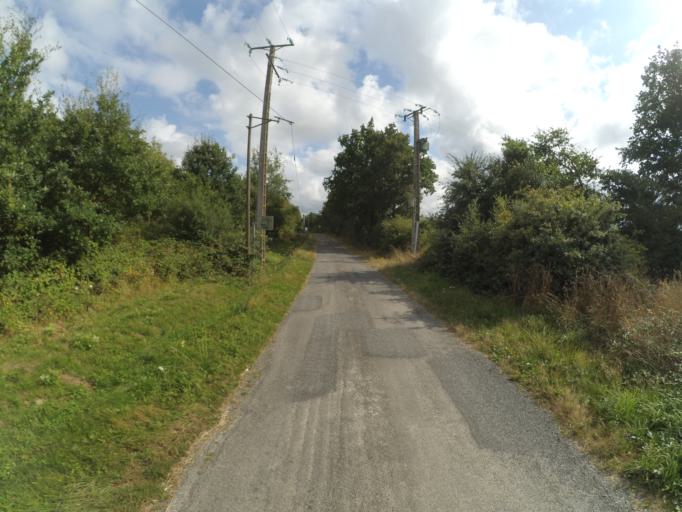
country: FR
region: Pays de la Loire
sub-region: Departement de la Loire-Atlantique
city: Vieillevigne
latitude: 46.9949
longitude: -1.4675
